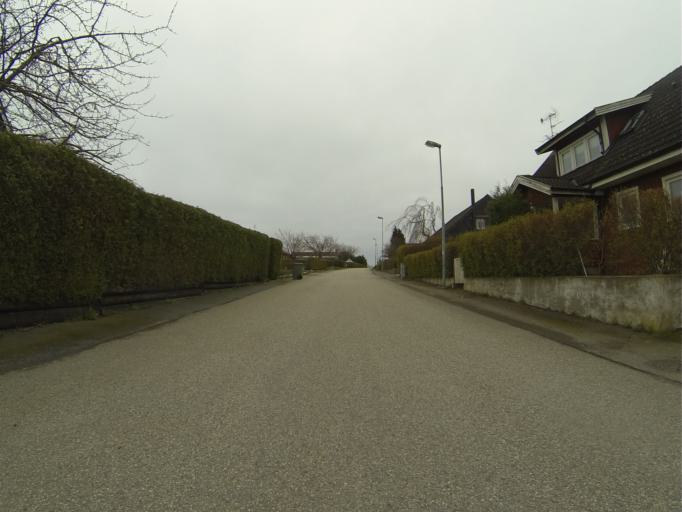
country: SE
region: Skane
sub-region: Simrishamns Kommun
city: Simrishamn
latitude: 55.5422
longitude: 14.3460
